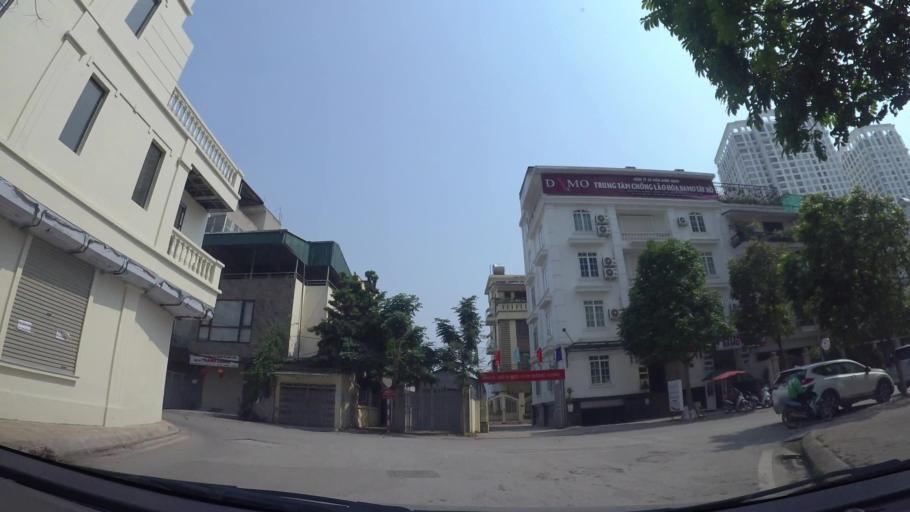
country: VN
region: Ha Noi
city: Tay Ho
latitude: 21.0855
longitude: 105.8134
